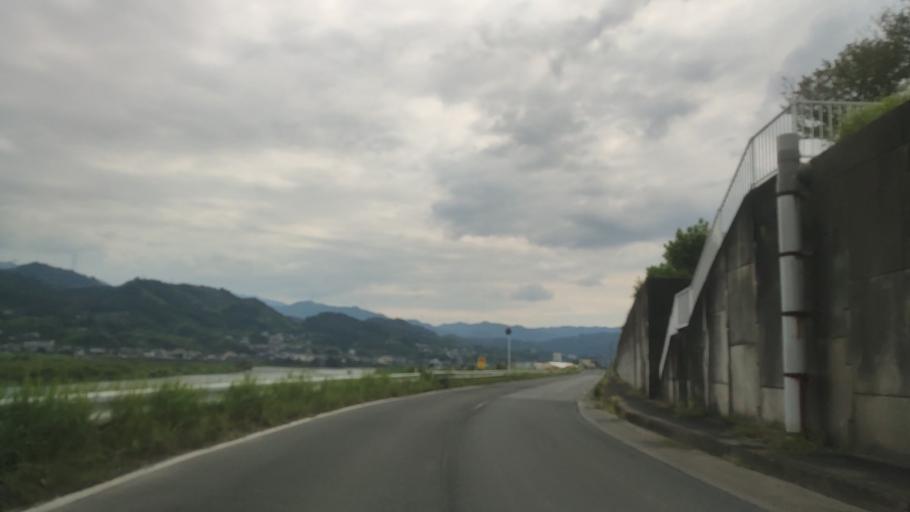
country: JP
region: Wakayama
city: Hashimoto
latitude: 34.3071
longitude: 135.5854
